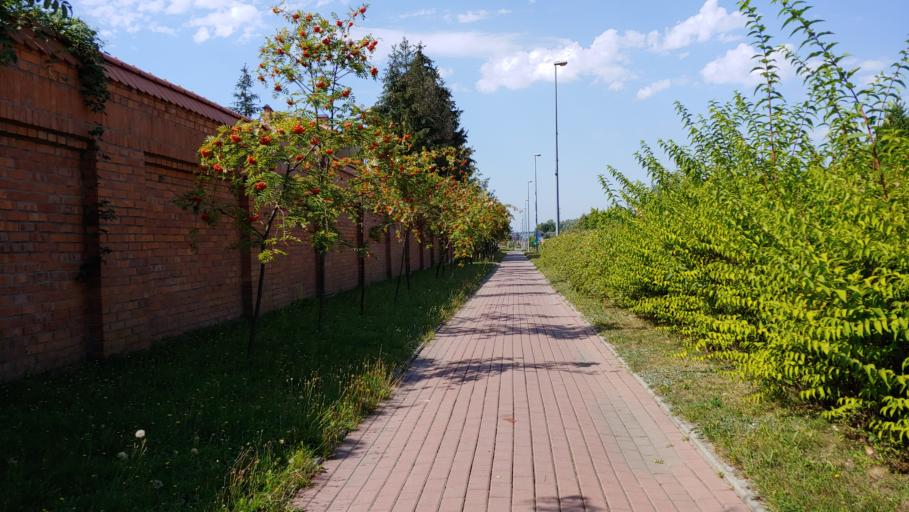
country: PL
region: Subcarpathian Voivodeship
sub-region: Powiat mielecki
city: Mielec
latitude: 50.2883
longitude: 21.4115
